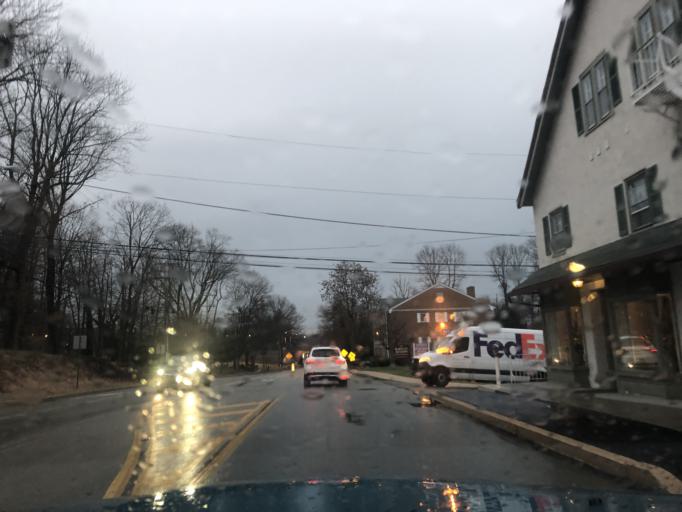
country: US
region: Pennsylvania
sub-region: Delaware County
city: Radnor
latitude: 40.0461
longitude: -75.3613
